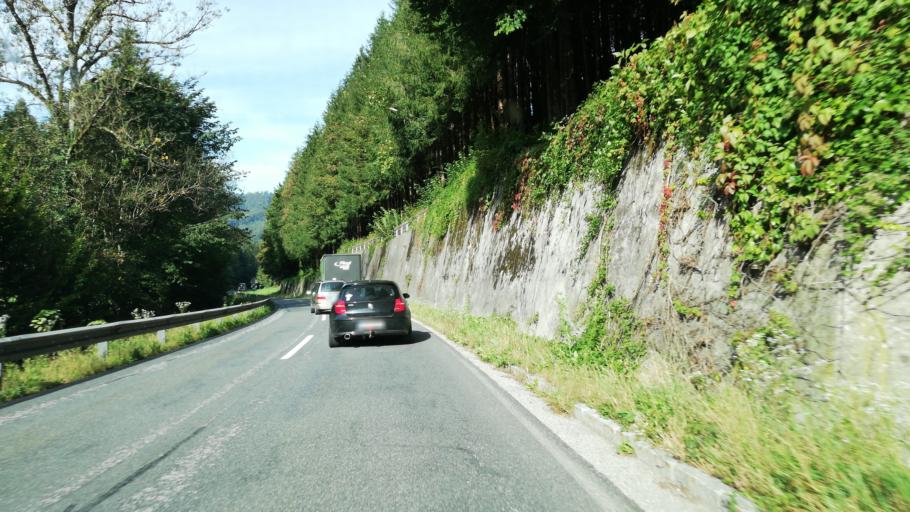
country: AT
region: Lower Austria
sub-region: Politischer Bezirk Amstetten
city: Behamberg
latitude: 47.9928
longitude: 14.5189
